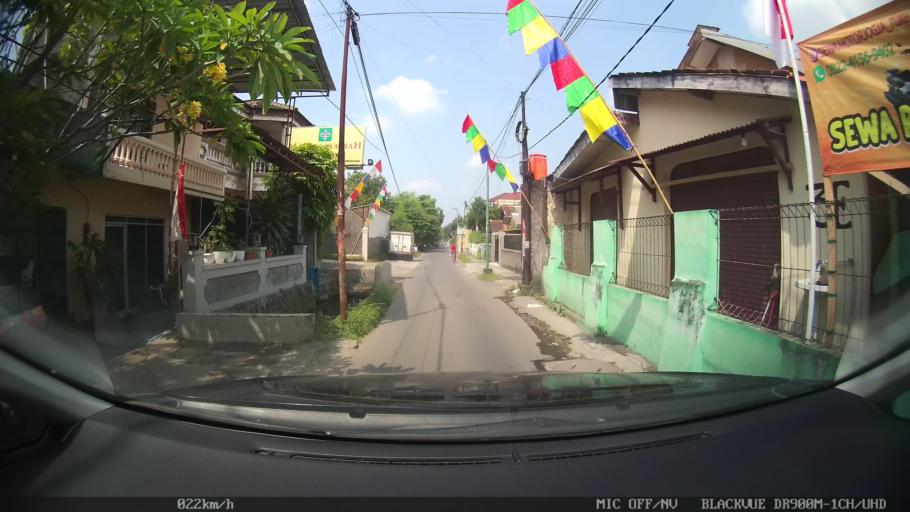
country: ID
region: Daerah Istimewa Yogyakarta
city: Yogyakarta
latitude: -7.7953
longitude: 110.3876
